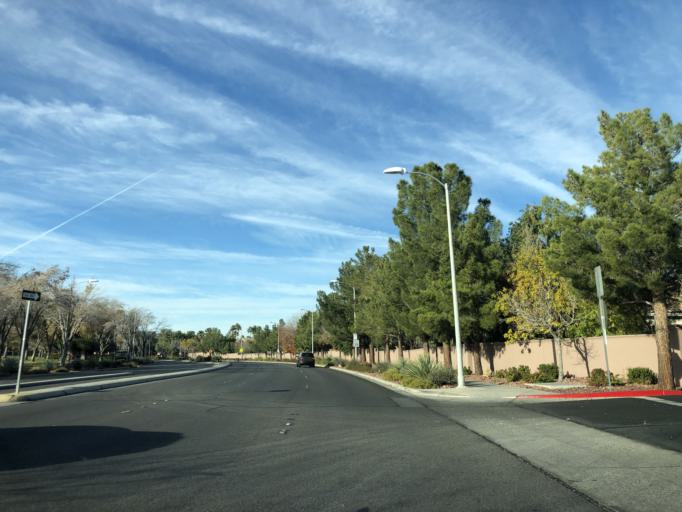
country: US
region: Nevada
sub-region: Clark County
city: Whitney
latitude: 36.0239
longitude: -115.0638
